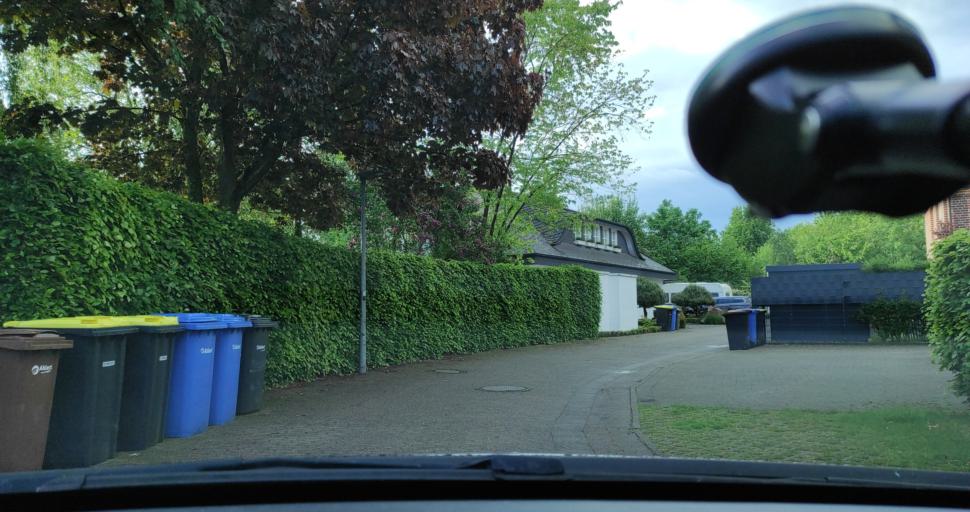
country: DE
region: North Rhine-Westphalia
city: Emsdetten
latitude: 52.1726
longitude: 7.5330
